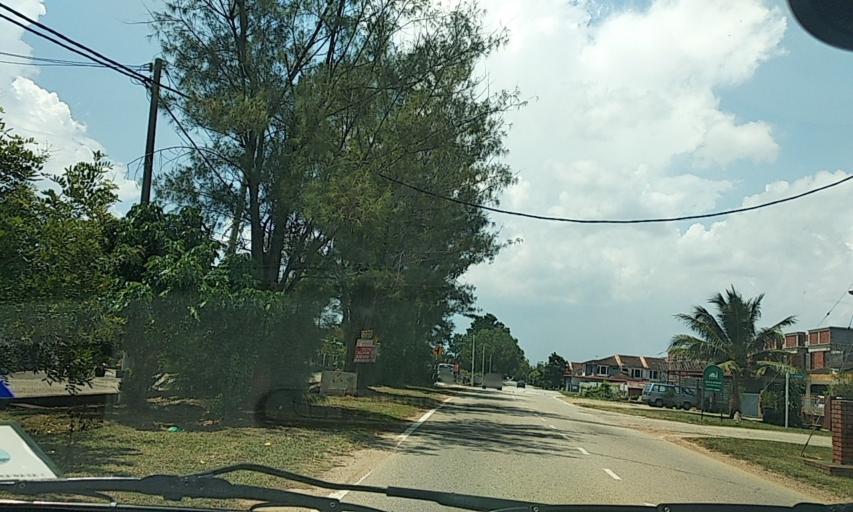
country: MY
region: Kedah
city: Sungai Petani
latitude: 5.6343
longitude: 100.4659
